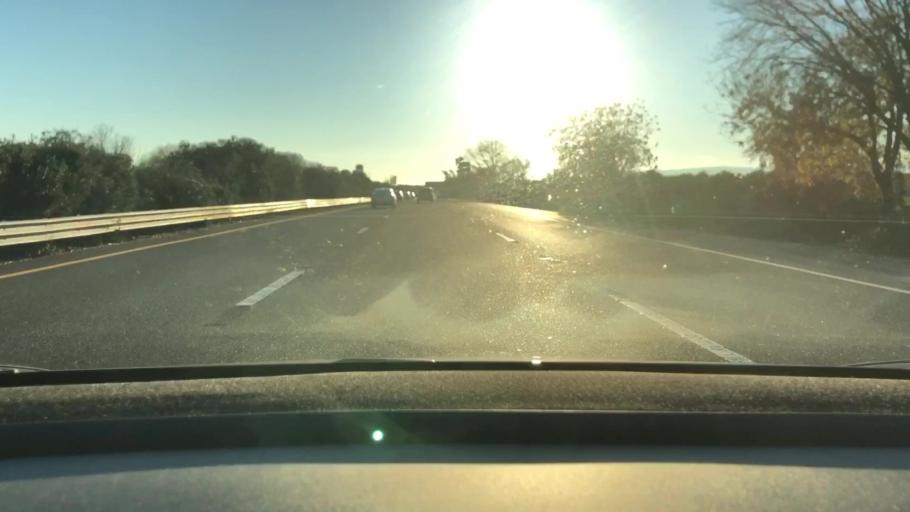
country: US
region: California
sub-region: Solano County
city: Dixon
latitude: 38.4805
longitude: -121.8156
